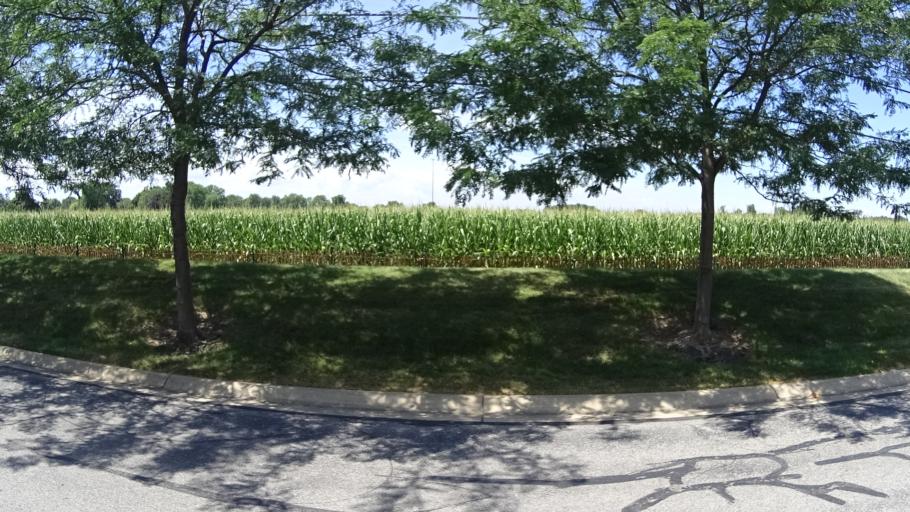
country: US
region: Ohio
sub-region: Erie County
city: Sandusky
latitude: 41.3978
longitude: -82.7008
